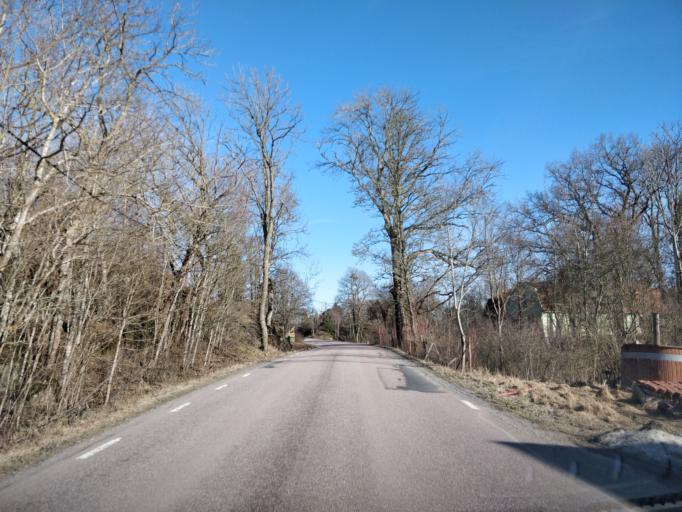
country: SE
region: Uppsala
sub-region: Enkopings Kommun
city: Orsundsbro
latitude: 59.7506
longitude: 17.2408
